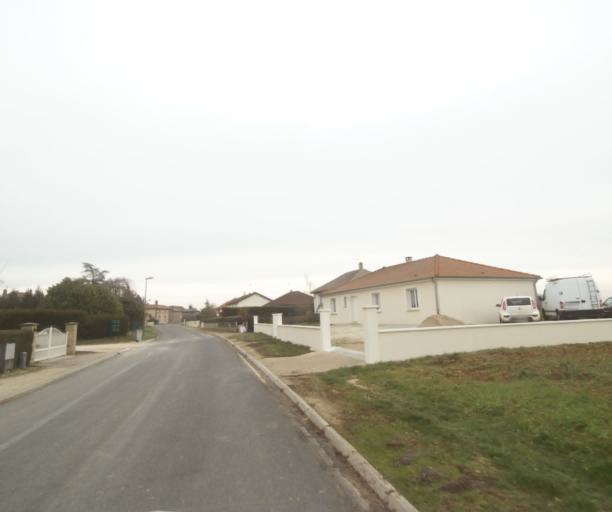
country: FR
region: Champagne-Ardenne
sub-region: Departement de la Haute-Marne
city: Villiers-en-Lieu
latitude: 48.6333
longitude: 4.8345
